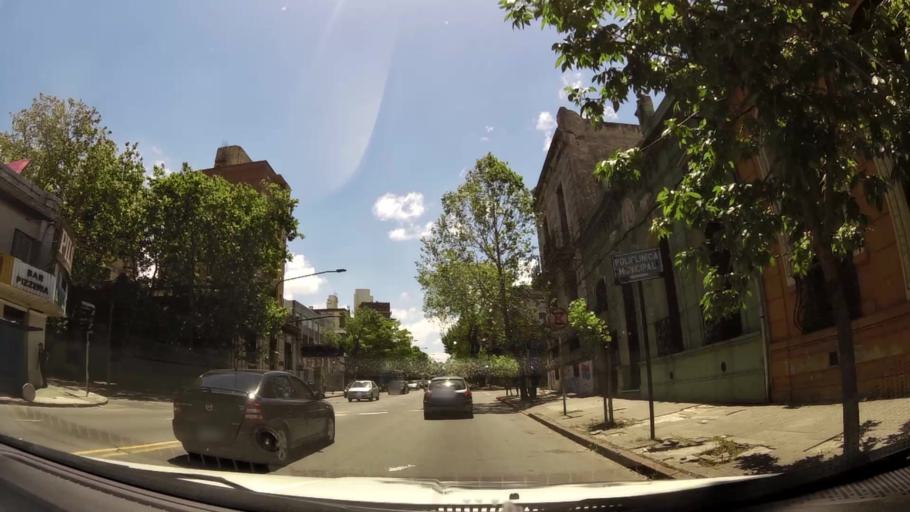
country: UY
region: Montevideo
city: Montevideo
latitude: -34.8797
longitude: -56.1958
